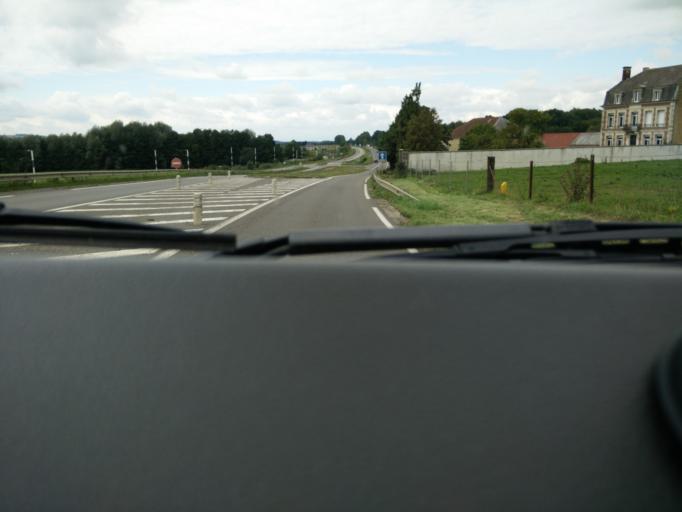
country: FR
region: Champagne-Ardenne
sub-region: Departement des Ardennes
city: Warcq
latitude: 49.7845
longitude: 4.6609
